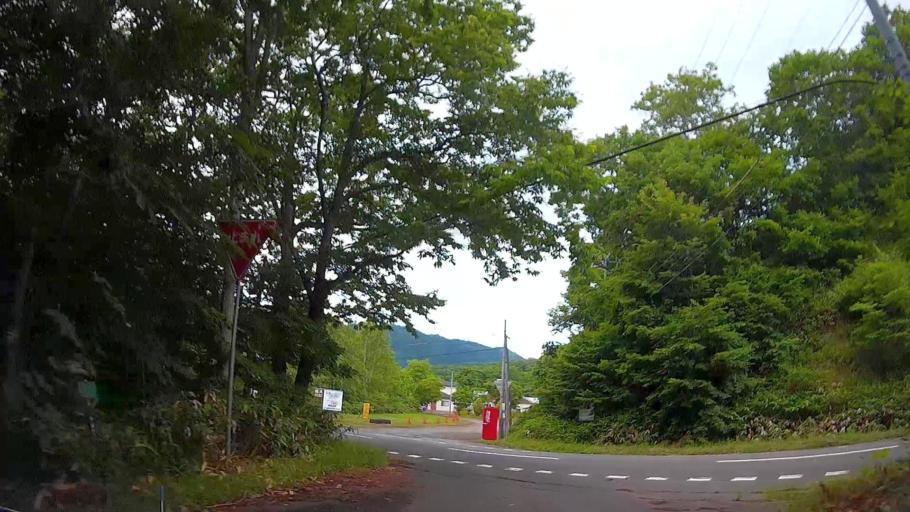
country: JP
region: Hokkaido
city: Nanae
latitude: 42.1241
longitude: 140.4555
